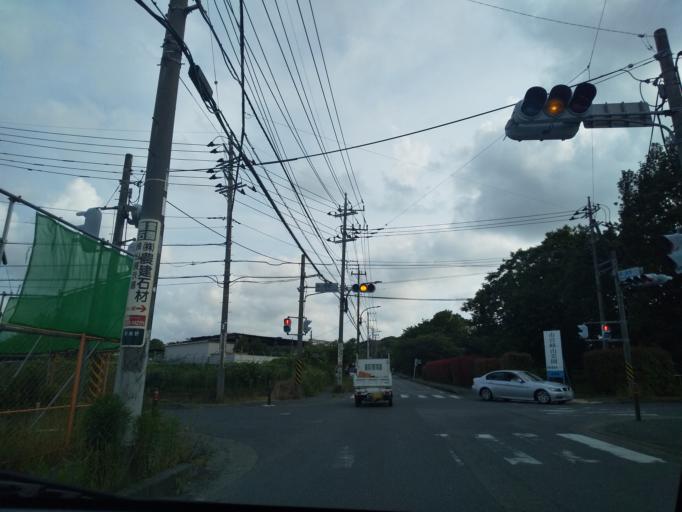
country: JP
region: Kanagawa
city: Zama
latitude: 35.5195
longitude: 139.3953
